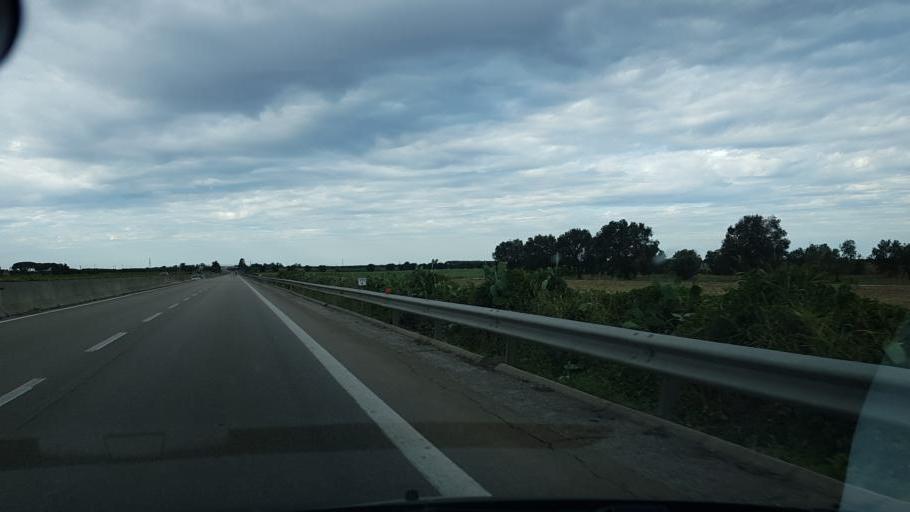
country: IT
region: Apulia
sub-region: Provincia di Brindisi
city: Tuturano
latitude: 40.5673
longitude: 17.9860
